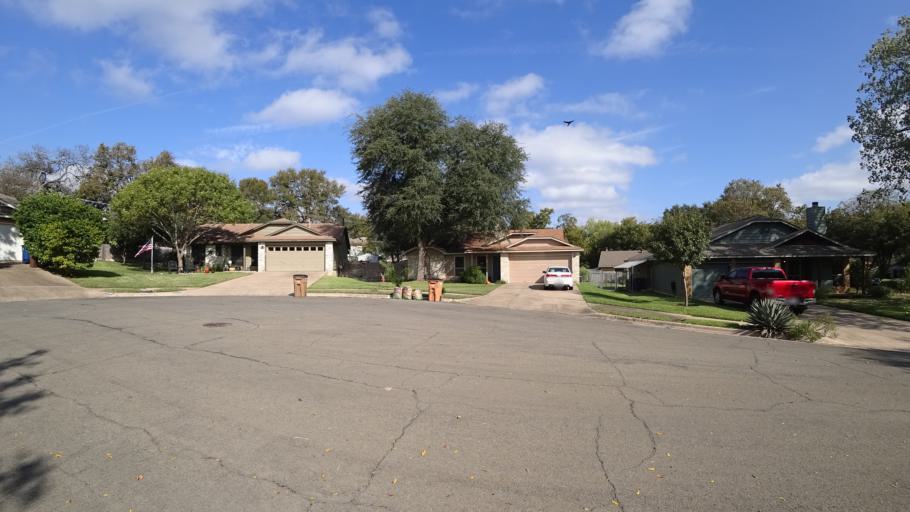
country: US
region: Texas
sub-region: Travis County
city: Shady Hollow
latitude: 30.1946
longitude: -97.8251
